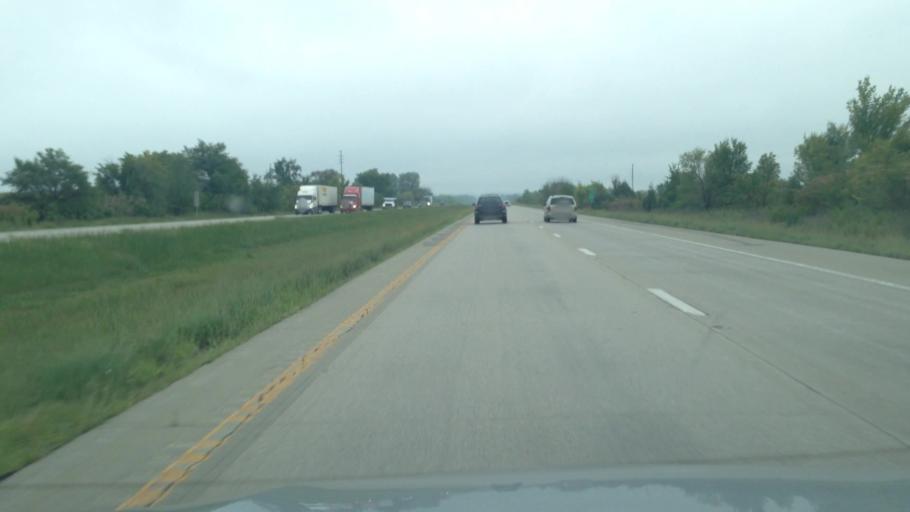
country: US
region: Missouri
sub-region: Clay County
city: Kearney
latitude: 39.4259
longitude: -94.3409
